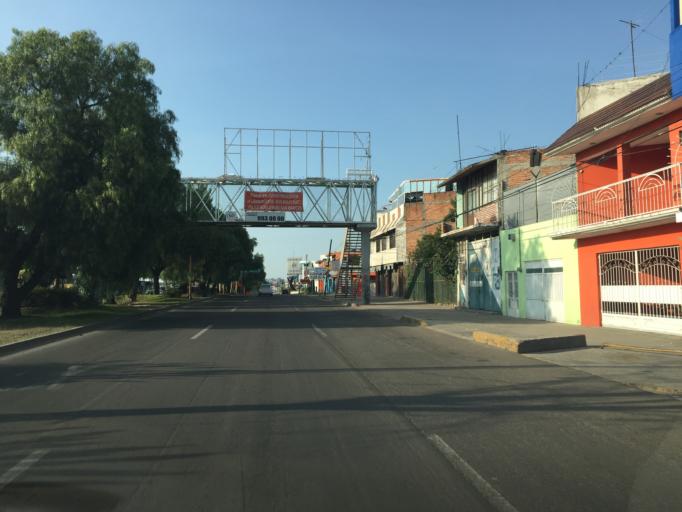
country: MX
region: Aguascalientes
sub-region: Aguascalientes
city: La Loma de los Negritos
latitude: 21.8640
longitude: -102.3174
